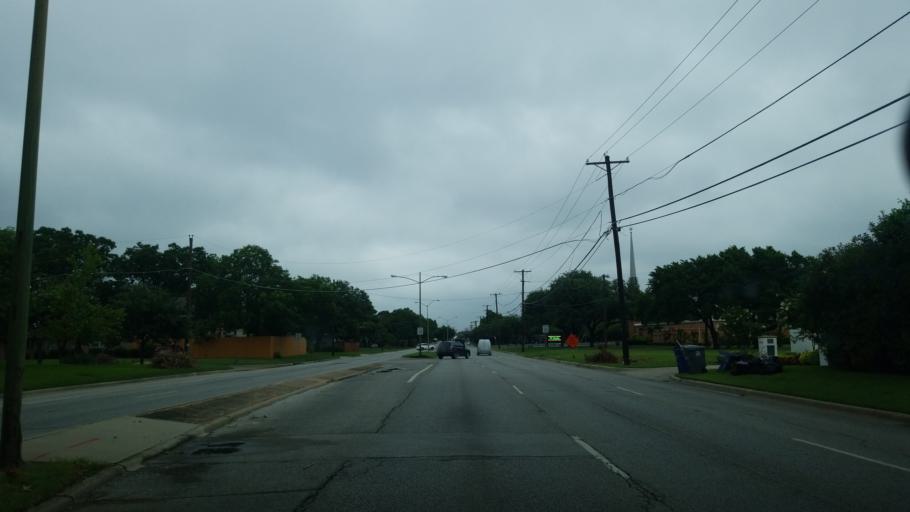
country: US
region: Texas
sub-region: Dallas County
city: Farmers Branch
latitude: 32.8890
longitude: -96.8561
